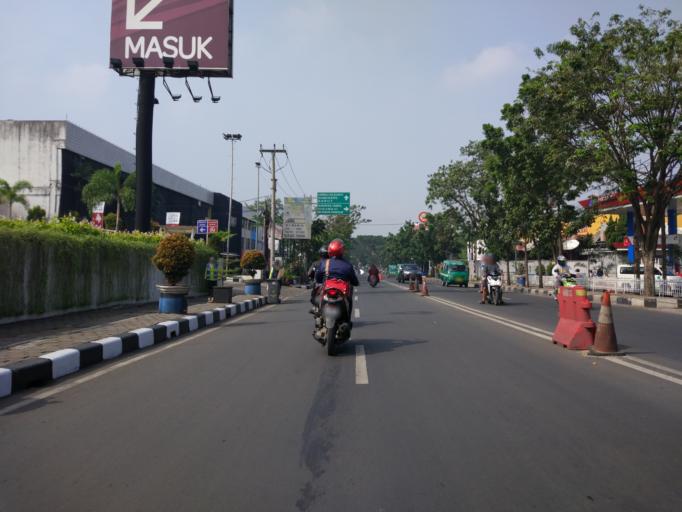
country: ID
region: West Java
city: Cileunyi
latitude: -6.9257
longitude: 107.7108
